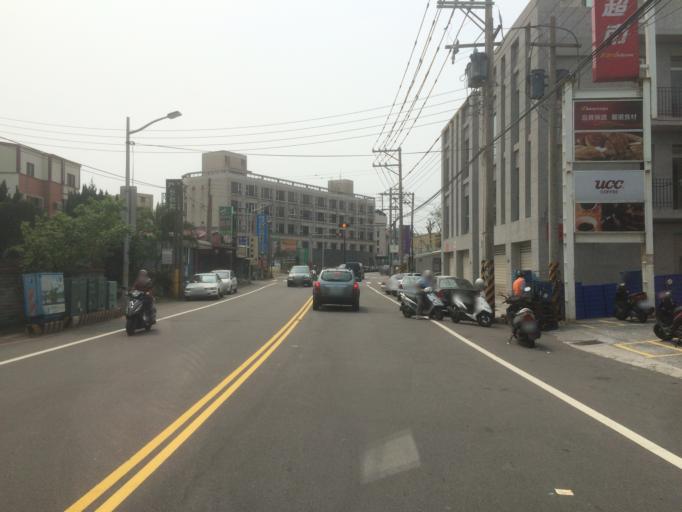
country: TW
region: Taiwan
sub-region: Hsinchu
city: Hsinchu
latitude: 24.7776
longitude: 120.9672
